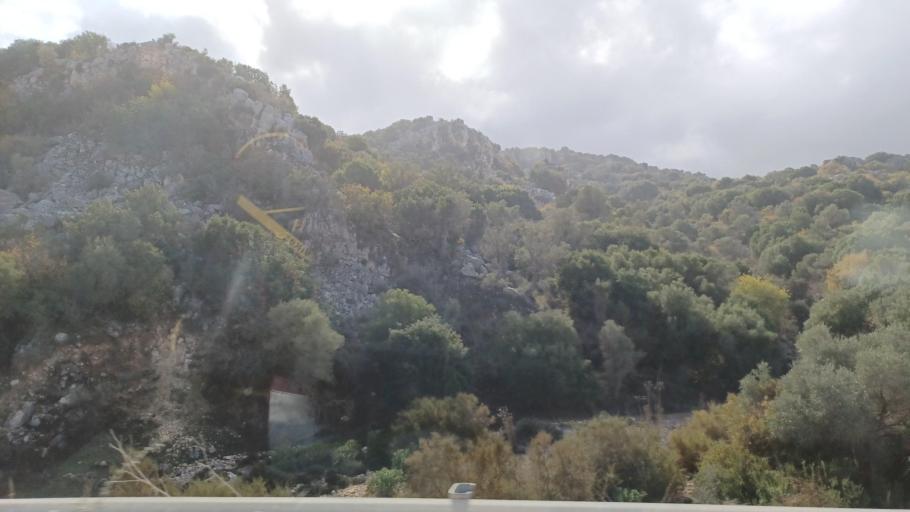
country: CY
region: Pafos
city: Polis
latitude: 34.9987
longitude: 32.4000
